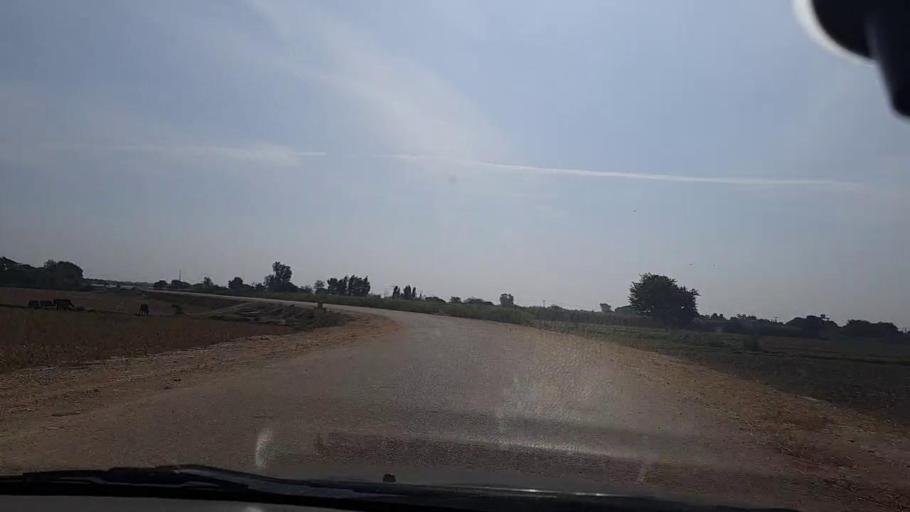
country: PK
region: Sindh
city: Mirpur Batoro
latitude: 24.7341
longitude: 68.2744
